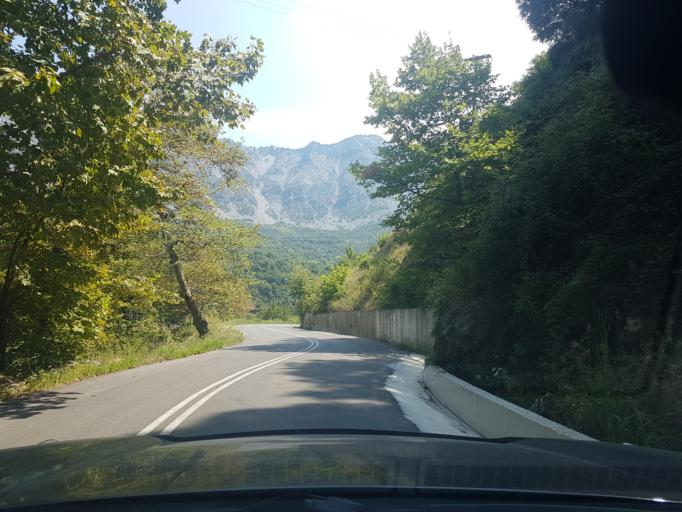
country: GR
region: Central Greece
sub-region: Nomos Evvoias
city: Kymi
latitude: 38.6286
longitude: 23.9445
